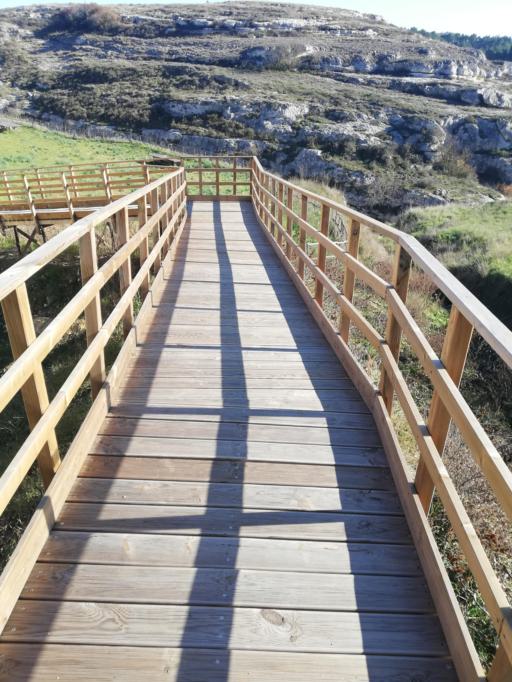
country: IT
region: Apulia
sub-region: Provincia di Bari
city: Gravina in Puglia
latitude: 40.8257
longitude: 16.4043
